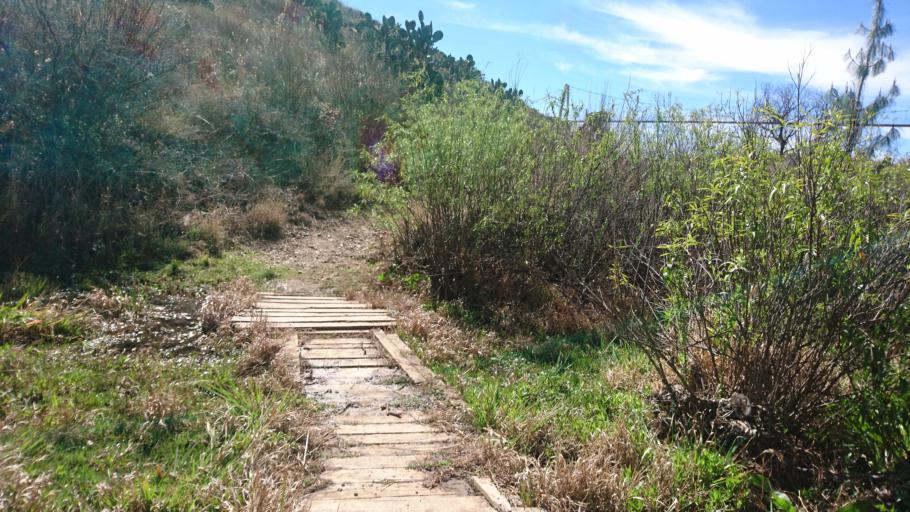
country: MX
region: Zacatecas
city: Guadalupe
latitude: 22.7784
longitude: -102.5450
